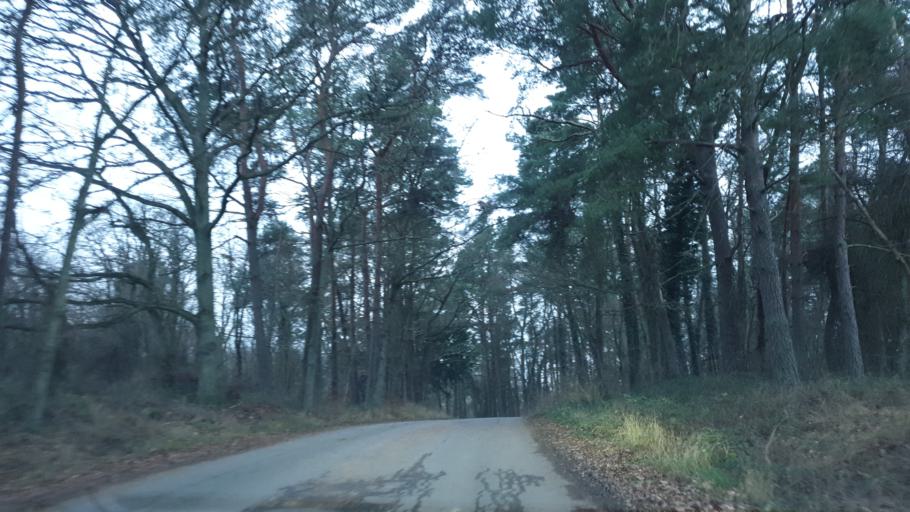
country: SE
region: Blekinge
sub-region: Karlskrona Kommun
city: Karlskrona
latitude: 56.1715
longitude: 15.5642
